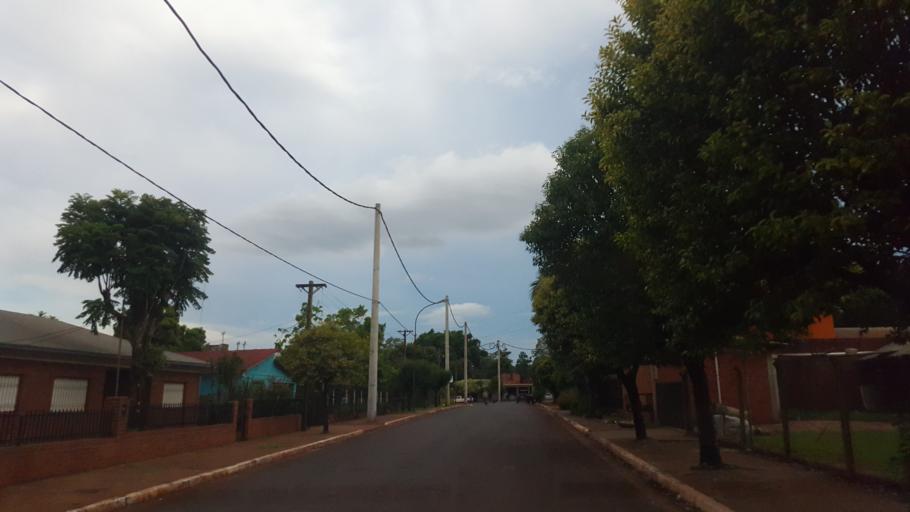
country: AR
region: Misiones
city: Jardin America
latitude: -27.0457
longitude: -55.2365
